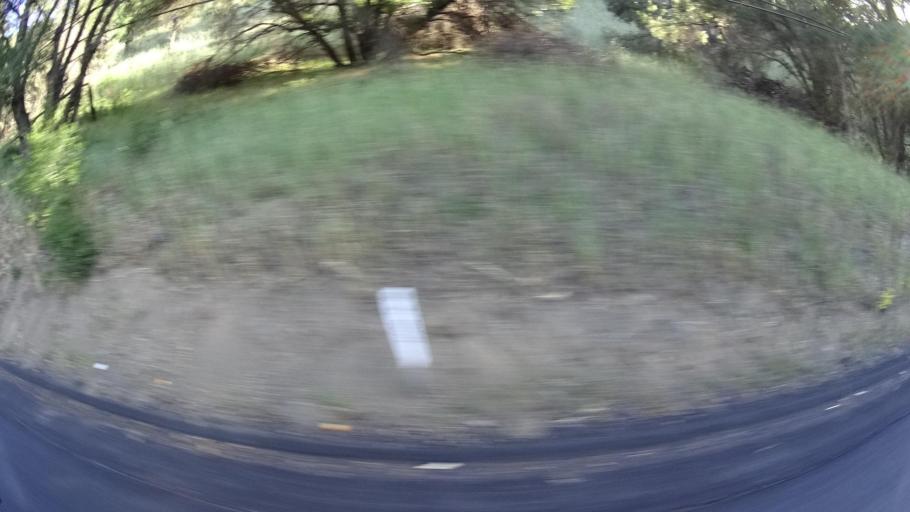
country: US
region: California
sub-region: Lake County
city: Upper Lake
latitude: 39.1666
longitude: -122.9722
